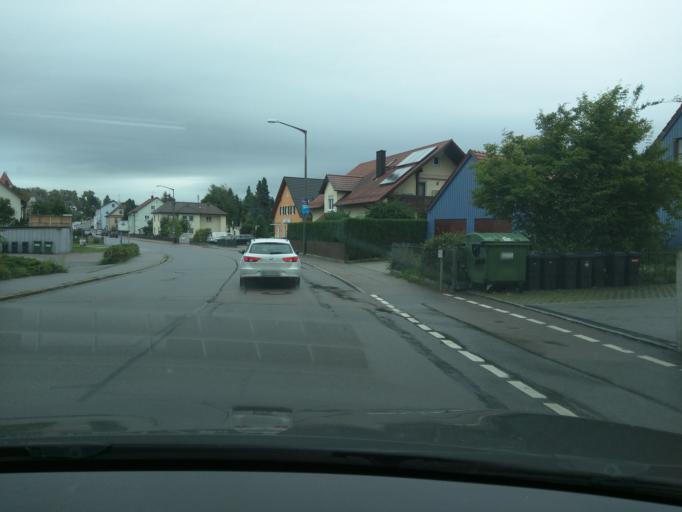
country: DE
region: Bavaria
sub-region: Upper Palatinate
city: Schwandorf in Bayern
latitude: 49.3391
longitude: 12.1220
